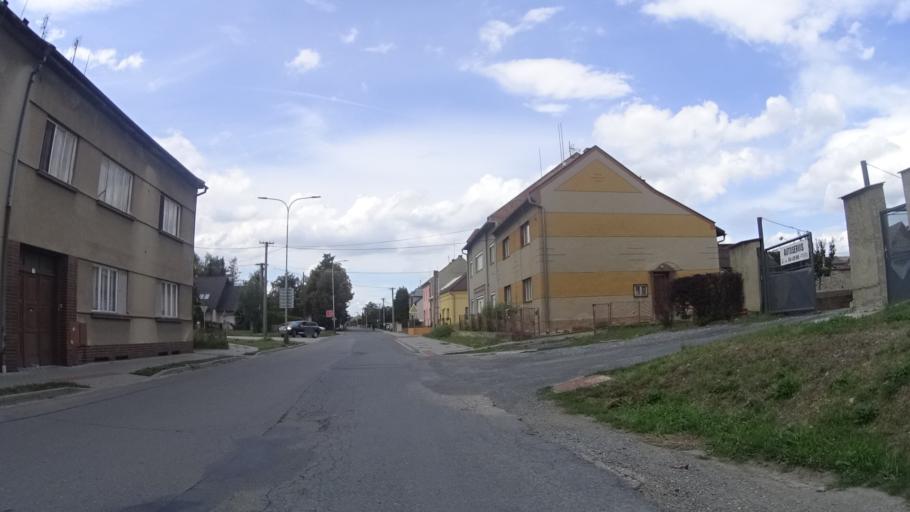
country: CZ
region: Olomoucky
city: Horka nad Moravou
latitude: 49.6379
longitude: 17.2057
